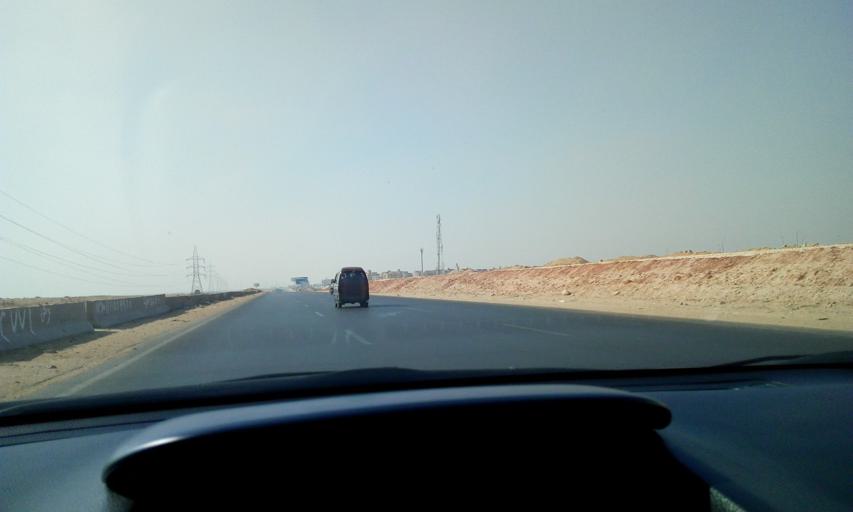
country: EG
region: Al Jizah
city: Madinat Sittah Uktubar
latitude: 29.9060
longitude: 31.0879
